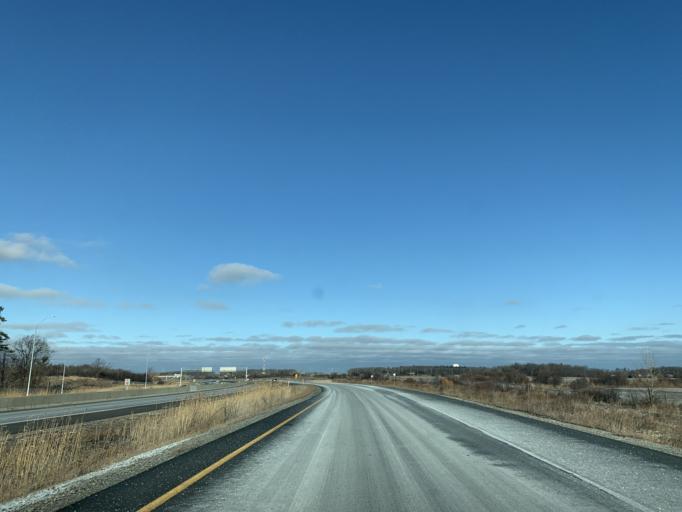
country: CA
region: Ontario
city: Oakville
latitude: 43.4864
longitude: -79.7628
